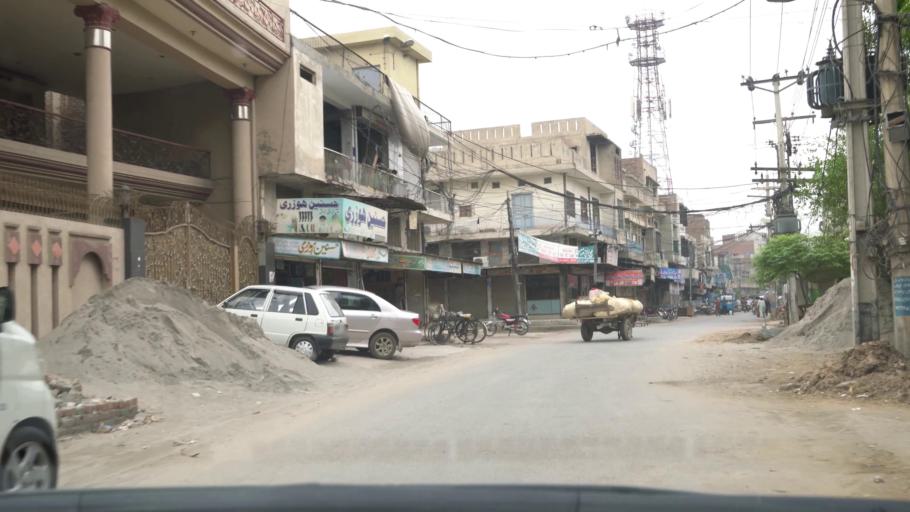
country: PK
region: Punjab
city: Faisalabad
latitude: 31.4218
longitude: 73.0688
